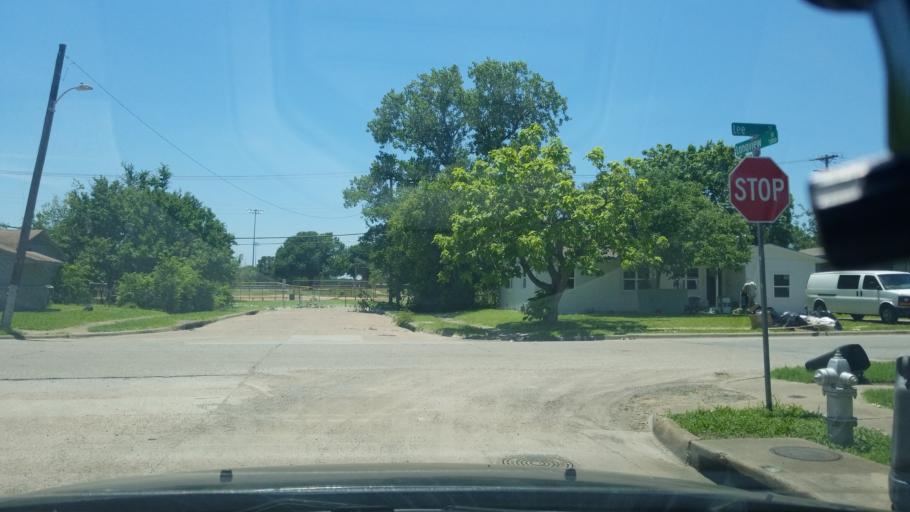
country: US
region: Texas
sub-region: Dallas County
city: Mesquite
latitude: 32.7797
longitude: -96.6131
